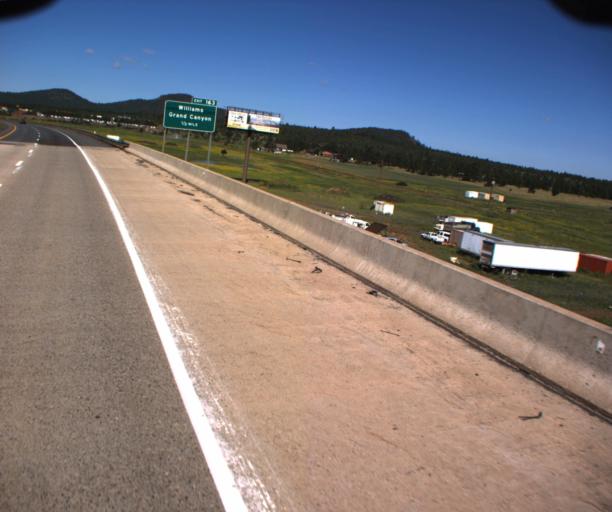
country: US
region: Arizona
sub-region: Coconino County
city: Williams
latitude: 35.2641
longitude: -112.1793
